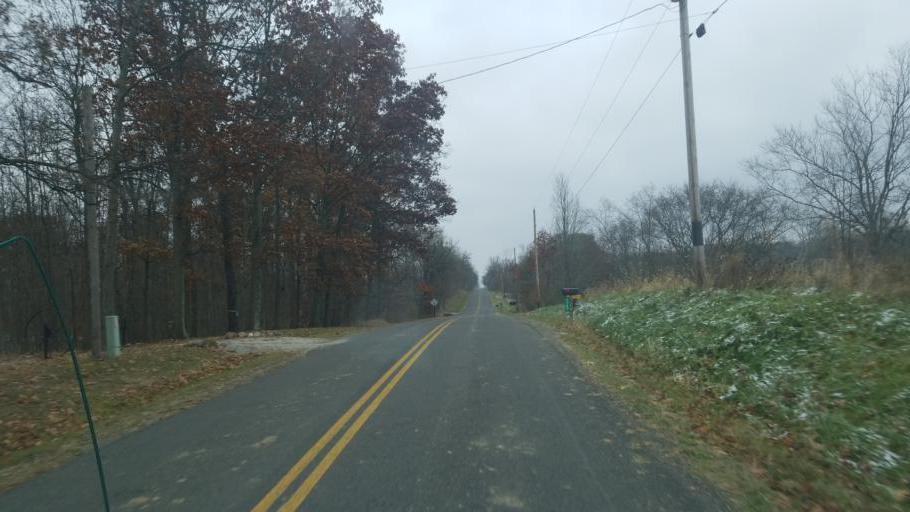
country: US
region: Ohio
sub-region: Medina County
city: Lodi
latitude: 41.1126
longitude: -82.0343
